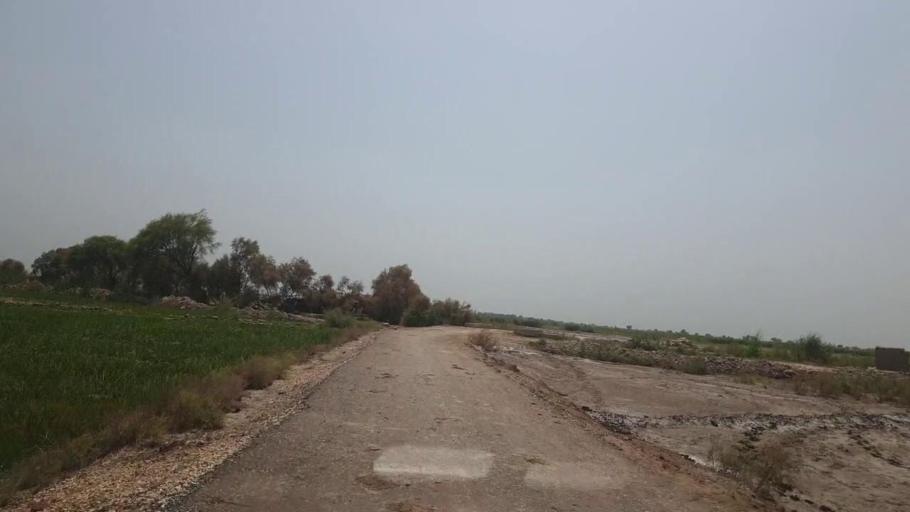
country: PK
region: Sindh
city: Garhi Yasin
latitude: 28.0566
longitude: 68.3162
